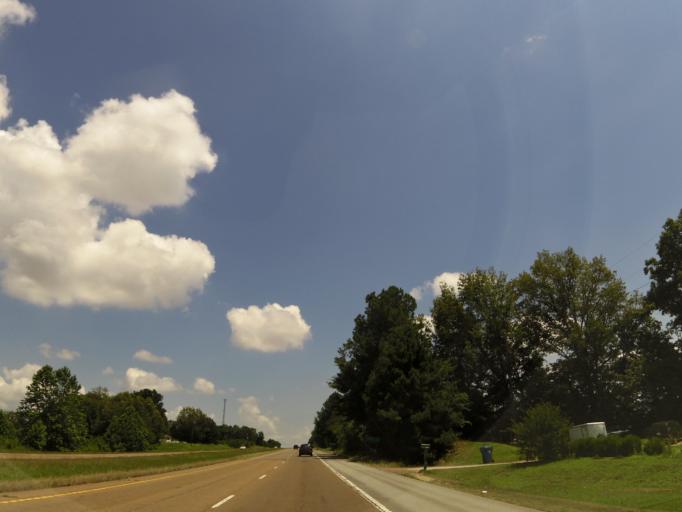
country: US
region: Tennessee
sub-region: Lauderdale County
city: Halls
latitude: 35.9138
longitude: -89.2679
